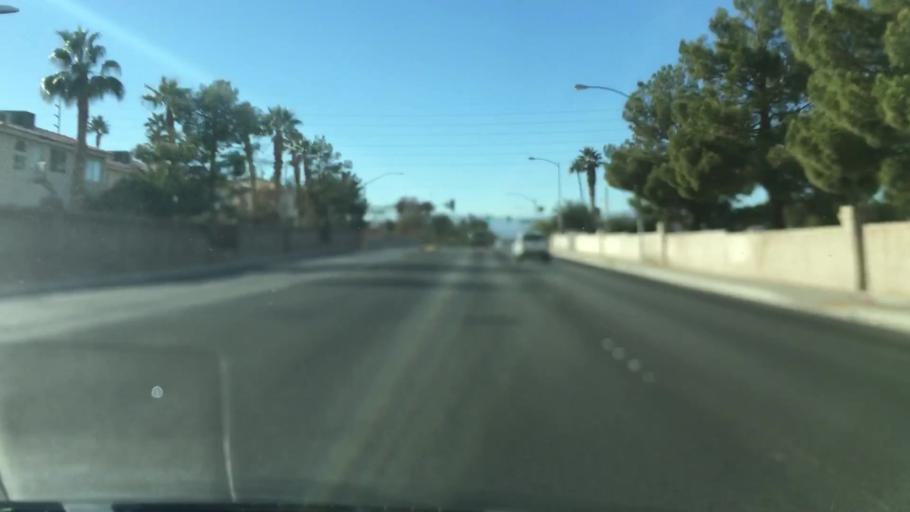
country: US
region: Nevada
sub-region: Clark County
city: Whitney
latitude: 36.0496
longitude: -115.1166
